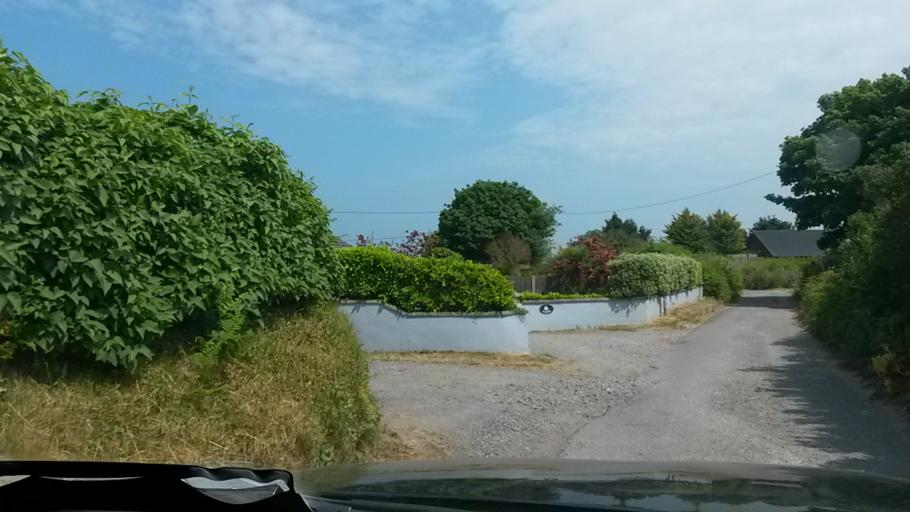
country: IE
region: Leinster
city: Portraine
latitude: 53.5003
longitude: -6.1158
